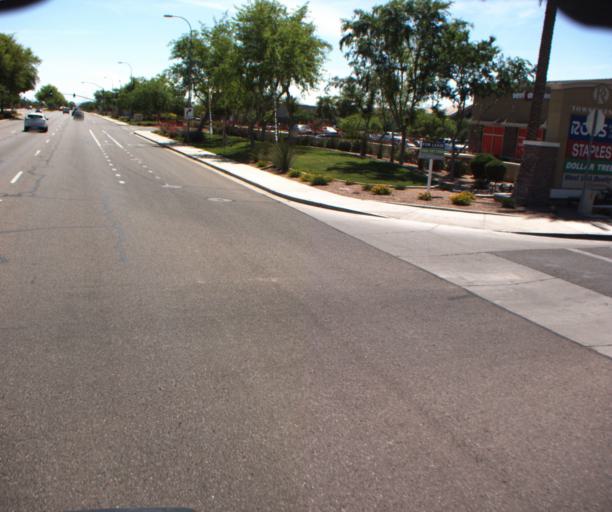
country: US
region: Arizona
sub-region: Maricopa County
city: Sun Lakes
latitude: 33.2458
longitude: -111.8413
